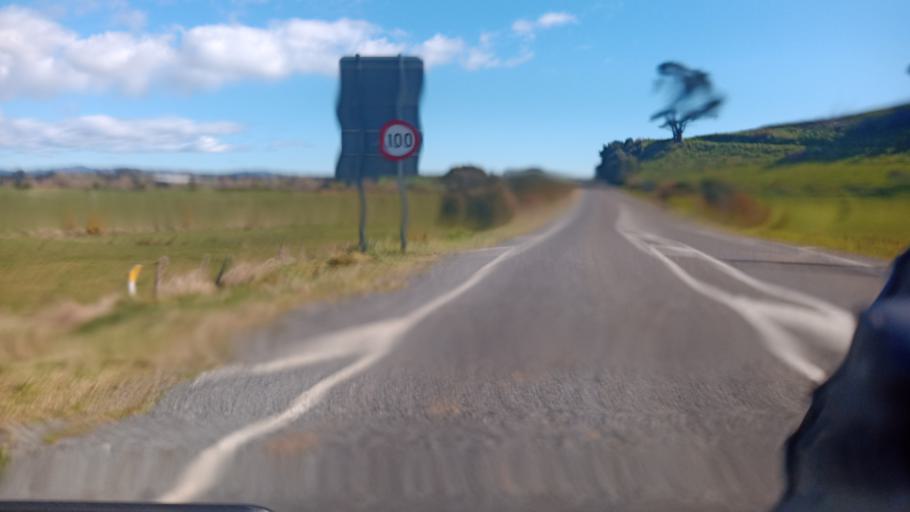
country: NZ
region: Bay of Plenty
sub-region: Opotiki District
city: Opotiki
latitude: -37.9901
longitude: 177.3478
